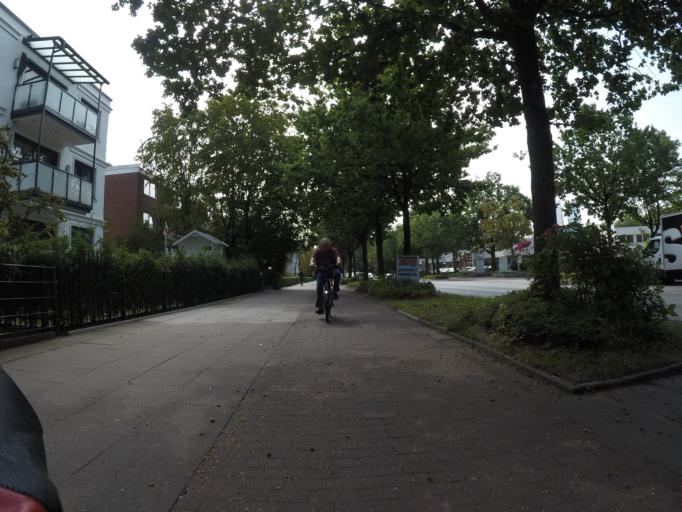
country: DE
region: Hamburg
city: Poppenbuettel
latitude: 53.6620
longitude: 10.0812
